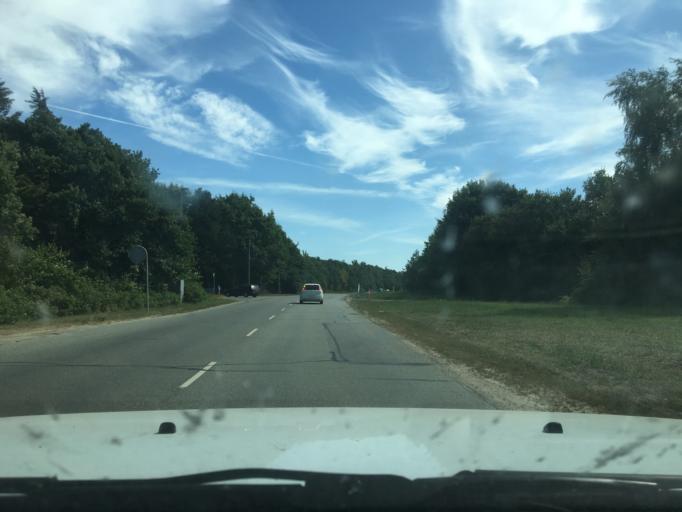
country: DK
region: Central Jutland
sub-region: Viborg Kommune
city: Viborg
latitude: 56.4678
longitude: 9.4468
